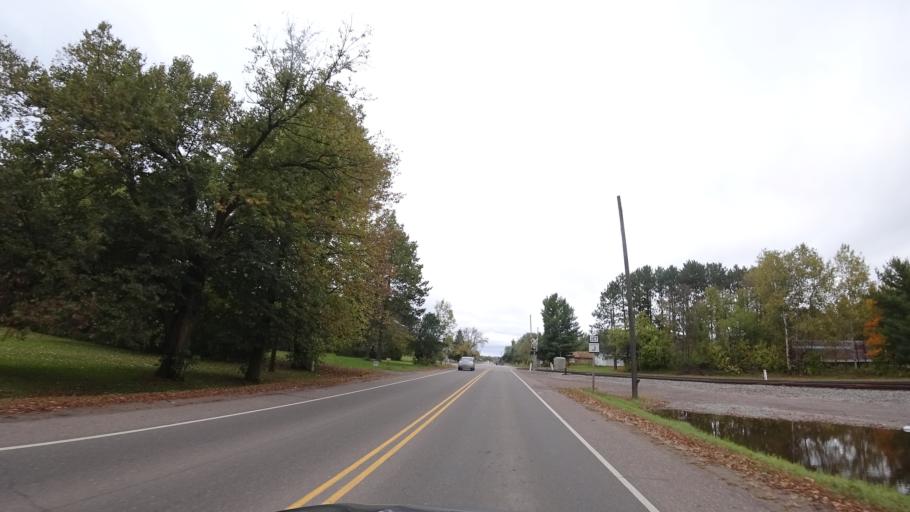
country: US
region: Wisconsin
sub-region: Rusk County
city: Ladysmith
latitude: 45.4727
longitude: -91.1107
